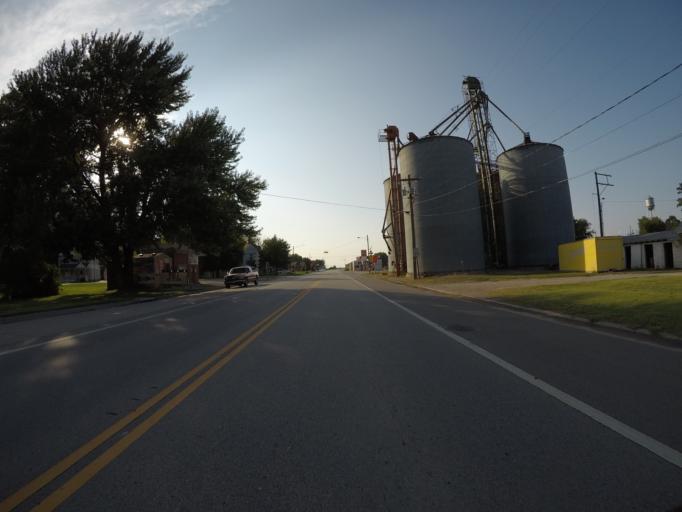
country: US
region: Kansas
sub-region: Shawnee County
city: Rossville
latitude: 39.1356
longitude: -95.9515
